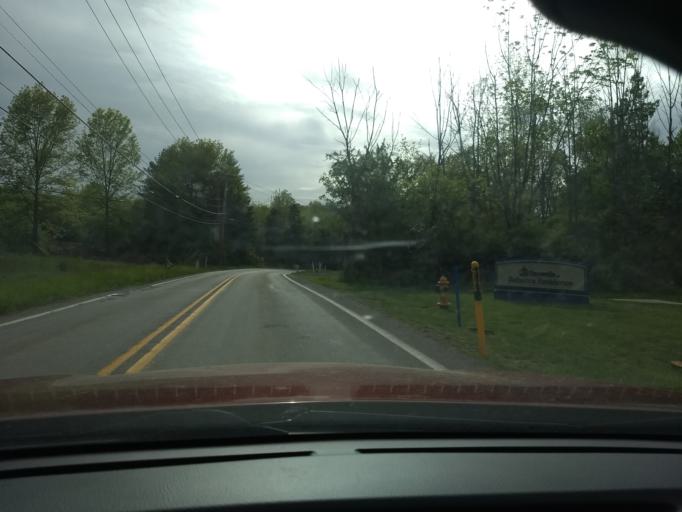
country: US
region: Pennsylvania
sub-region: Allegheny County
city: Russellton
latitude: 40.6004
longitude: -79.8946
